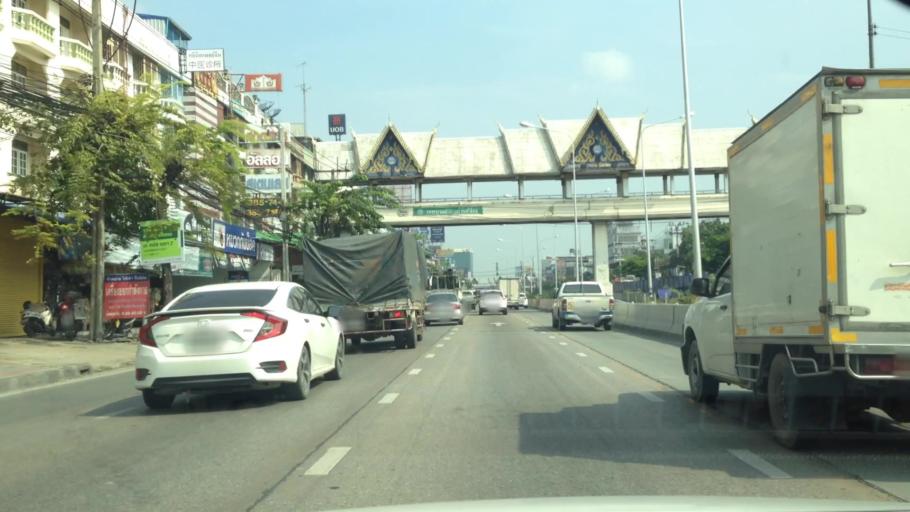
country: TH
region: Bangkok
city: Bang Na
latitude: 13.6376
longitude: 100.6326
